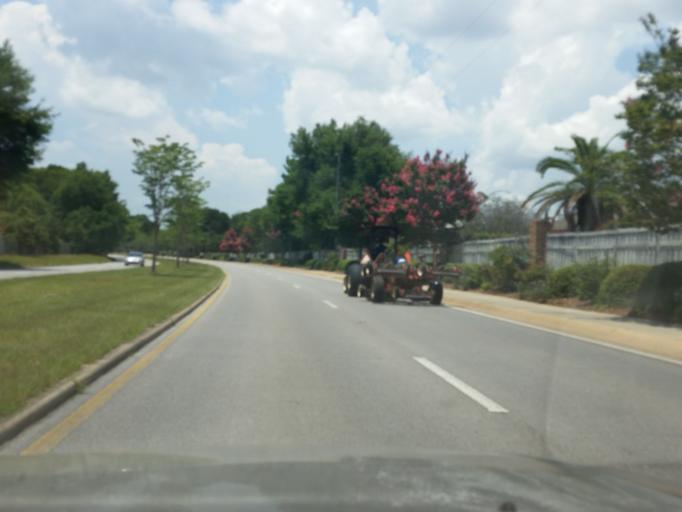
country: US
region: Florida
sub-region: Escambia County
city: East Pensacola Heights
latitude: 30.4624
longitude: -87.1903
